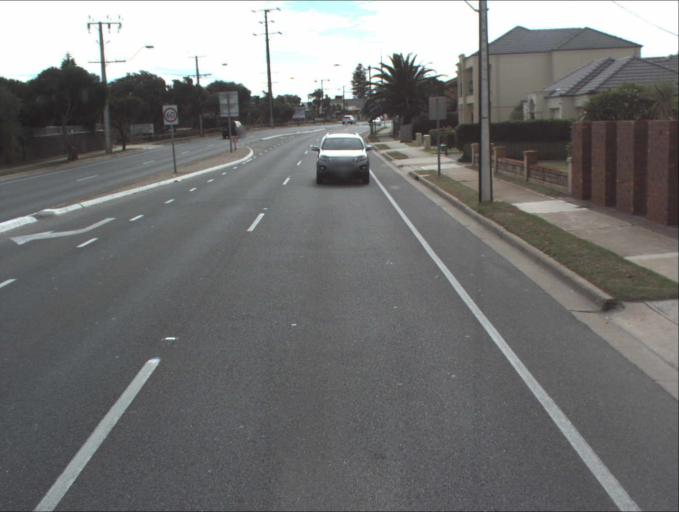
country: AU
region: South Australia
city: Port Adelaide
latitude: -34.8523
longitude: 138.4790
